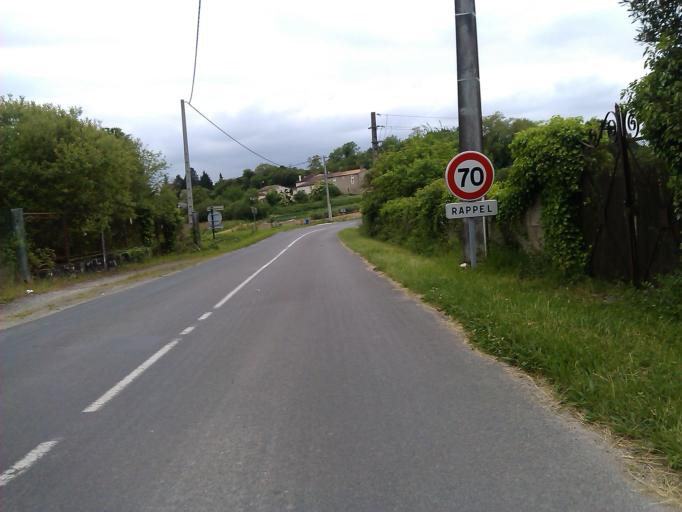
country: FR
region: Poitou-Charentes
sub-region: Departement de la Charente
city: Chateauneuf-sur-Charente
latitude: 45.5968
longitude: -0.0369
